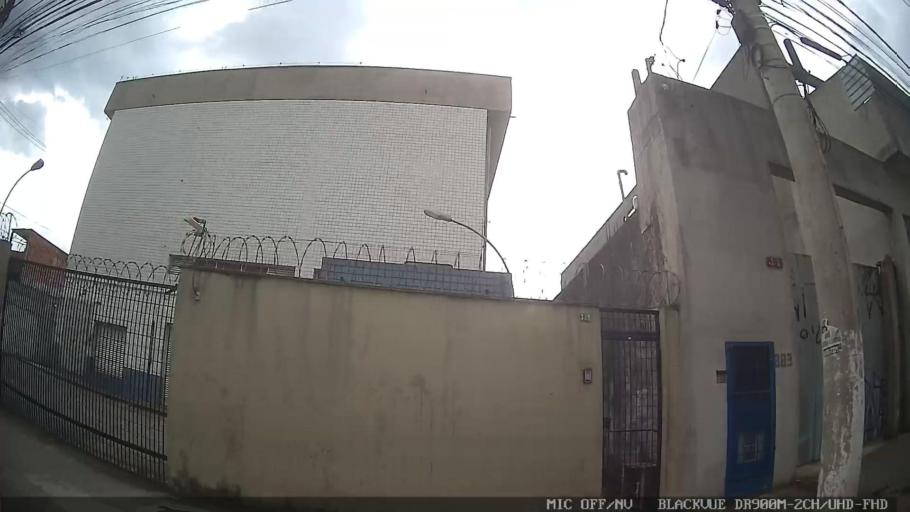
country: BR
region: Sao Paulo
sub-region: Itaquaquecetuba
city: Itaquaquecetuba
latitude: -23.4636
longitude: -46.3264
